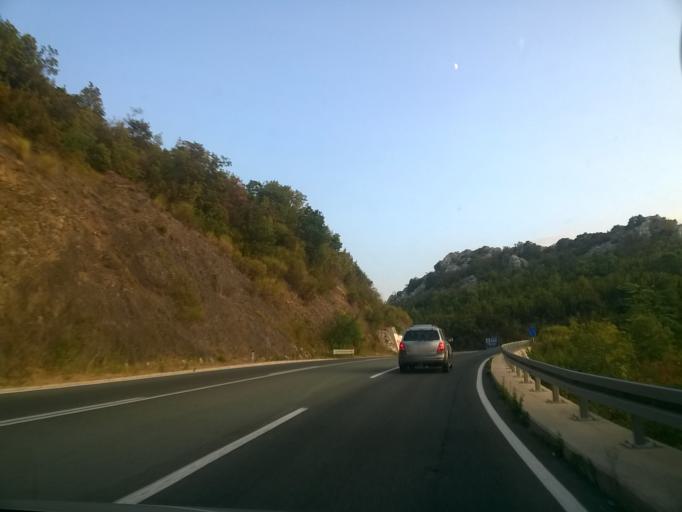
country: ME
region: Bar
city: Sutomore
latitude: 42.1769
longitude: 18.9973
